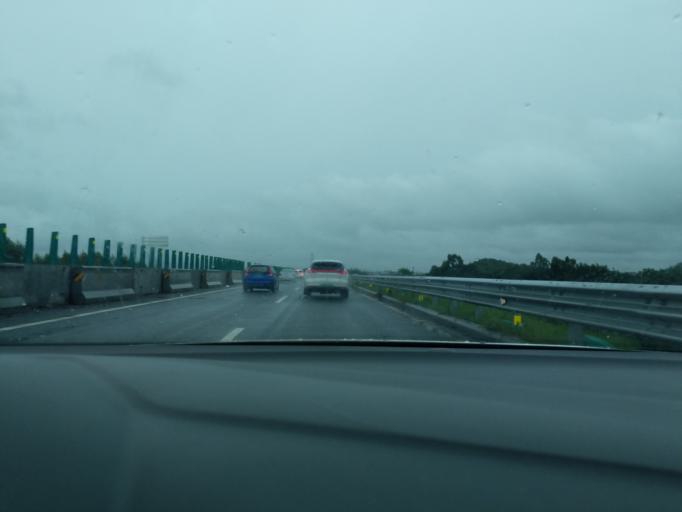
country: CN
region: Guangdong
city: Yueshan
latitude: 22.4617
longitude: 112.6898
